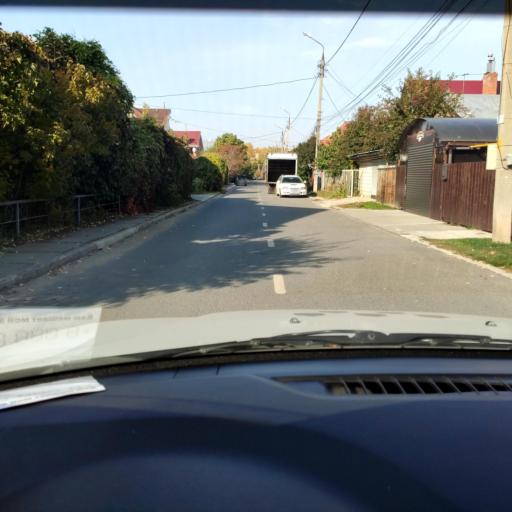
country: RU
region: Samara
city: Tol'yatti
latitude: 53.5354
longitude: 49.3880
